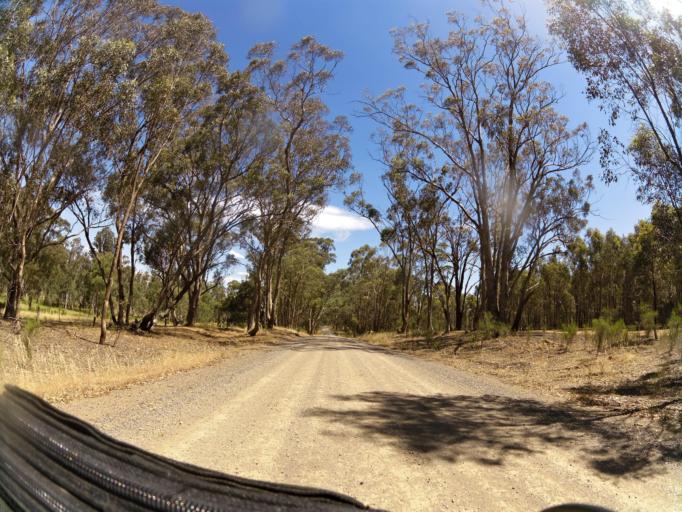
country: AU
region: Victoria
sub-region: Campaspe
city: Kyabram
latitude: -36.8226
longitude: 145.0791
